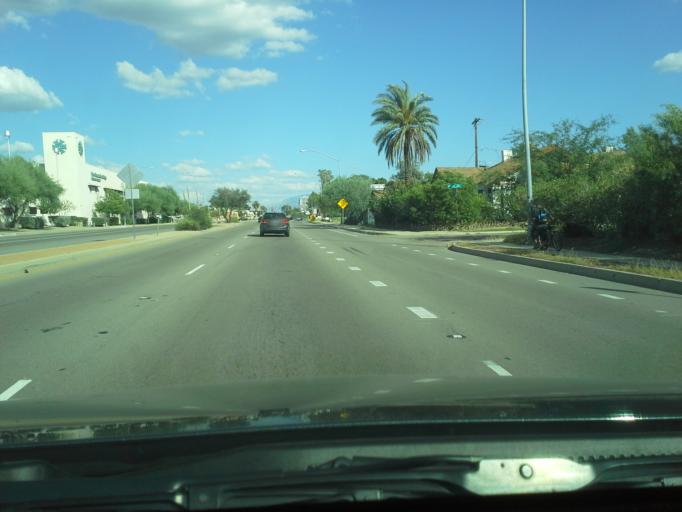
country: US
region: Arizona
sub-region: Pima County
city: South Tucson
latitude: 32.2359
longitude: -110.9745
